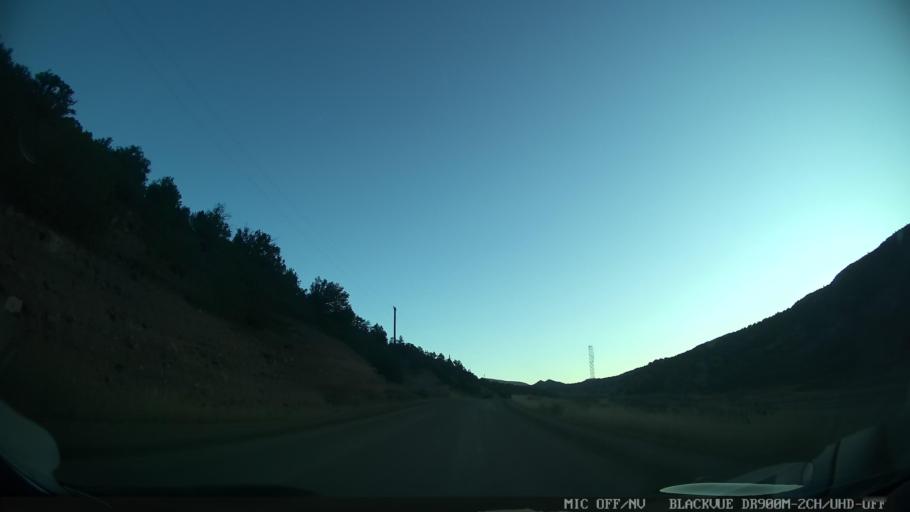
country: US
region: Colorado
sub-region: Eagle County
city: Edwards
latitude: 39.8867
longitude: -106.6239
